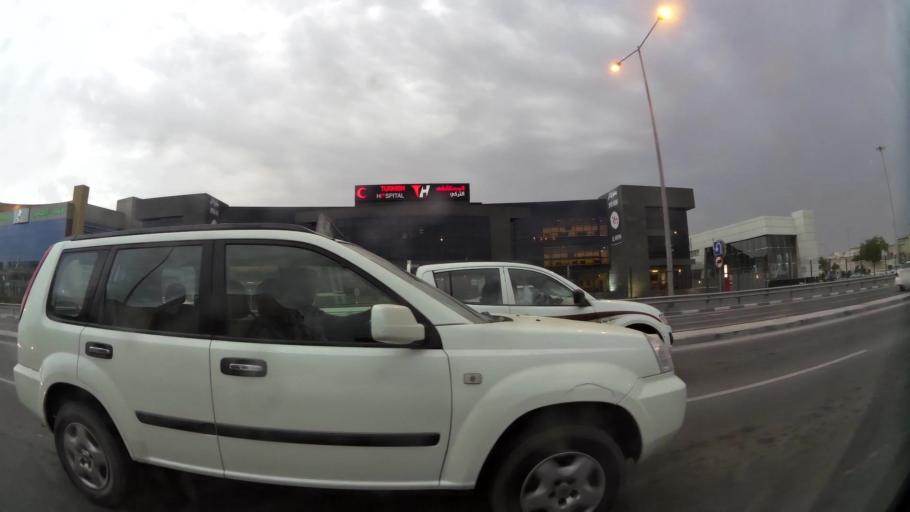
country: QA
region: Baladiyat ad Dawhah
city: Doha
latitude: 25.2675
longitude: 51.5152
